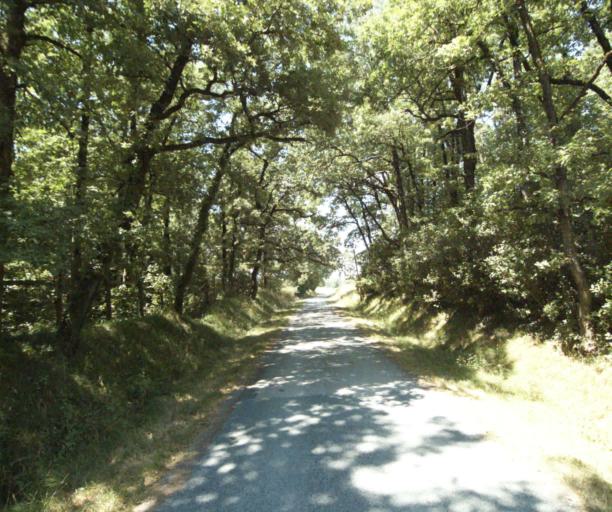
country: FR
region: Midi-Pyrenees
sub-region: Departement de la Haute-Garonne
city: Saint-Felix-Lauragais
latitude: 43.4740
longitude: 1.8685
